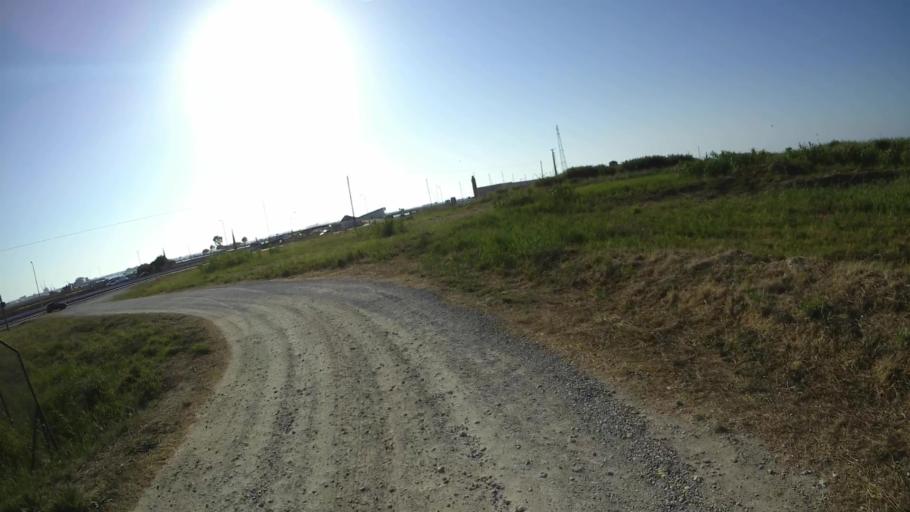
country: PT
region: Aveiro
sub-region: Aveiro
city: Aveiro
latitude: 40.6453
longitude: -8.6603
